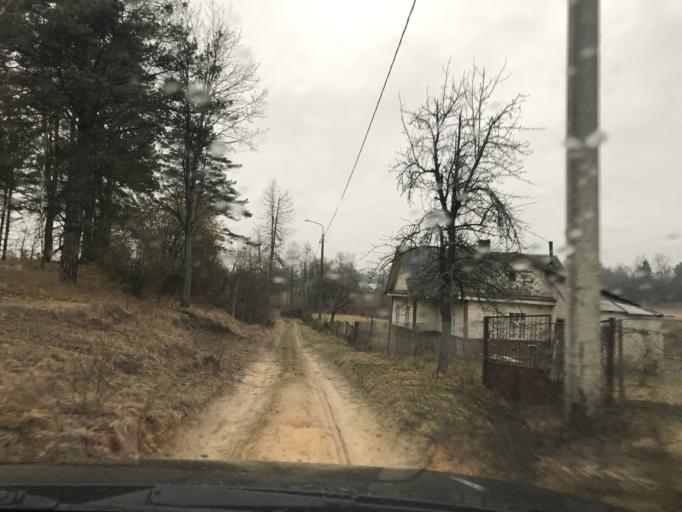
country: LT
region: Alytaus apskritis
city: Druskininkai
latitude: 53.9068
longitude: 24.1785
